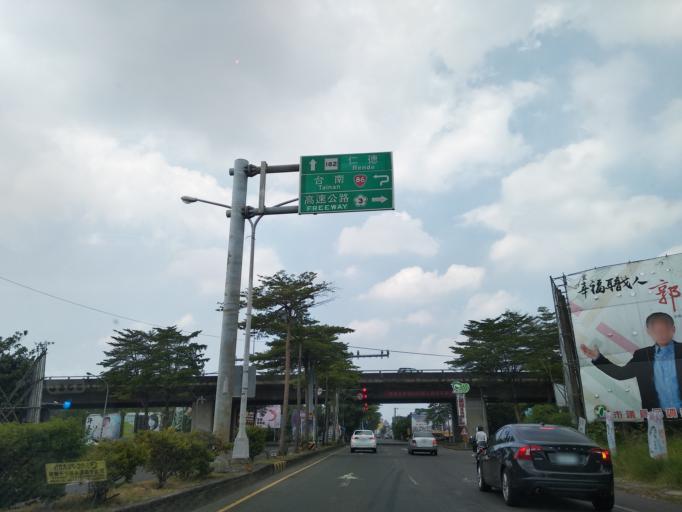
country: TW
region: Taiwan
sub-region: Tainan
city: Tainan
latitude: 22.9636
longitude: 120.3104
